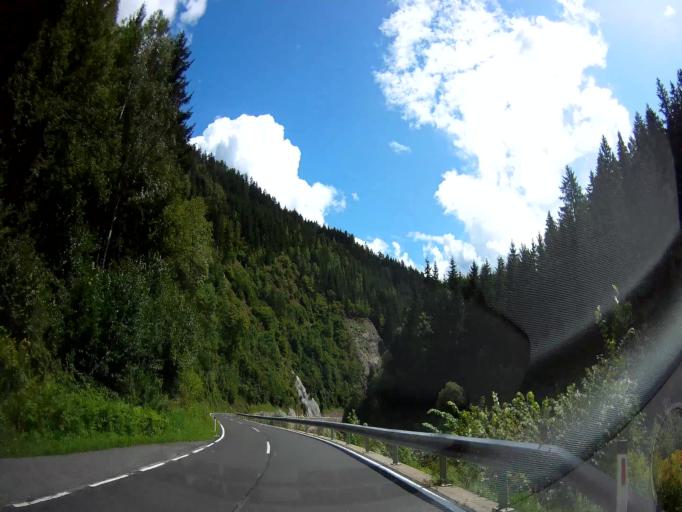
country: AT
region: Carinthia
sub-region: Politischer Bezirk Spittal an der Drau
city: Seeboden
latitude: 46.8504
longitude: 13.5011
